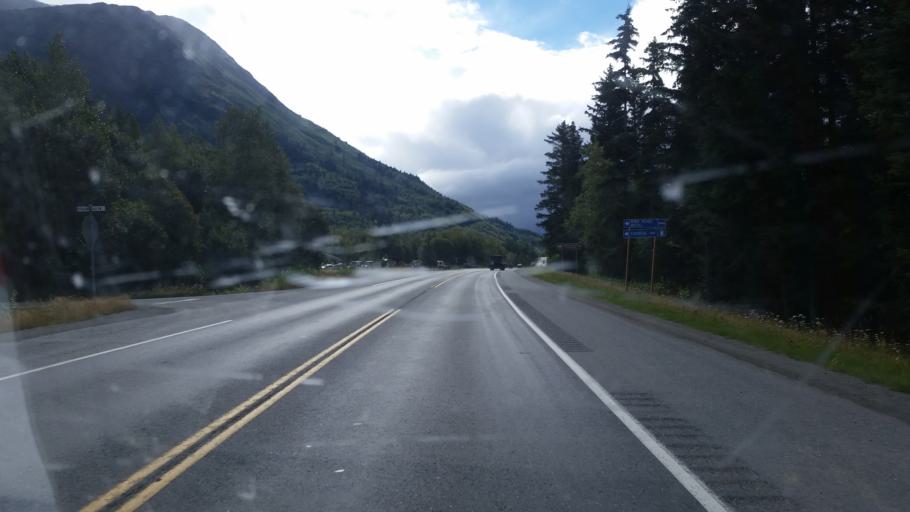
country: US
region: Alaska
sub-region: Anchorage Municipality
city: Girdwood
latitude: 60.9704
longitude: -149.4524
